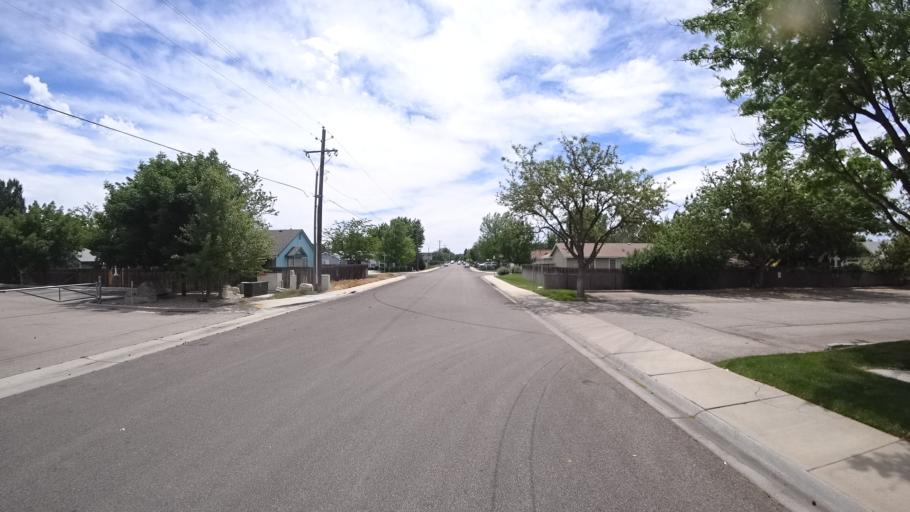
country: US
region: Idaho
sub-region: Ada County
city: Garden City
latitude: 43.6179
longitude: -116.3092
